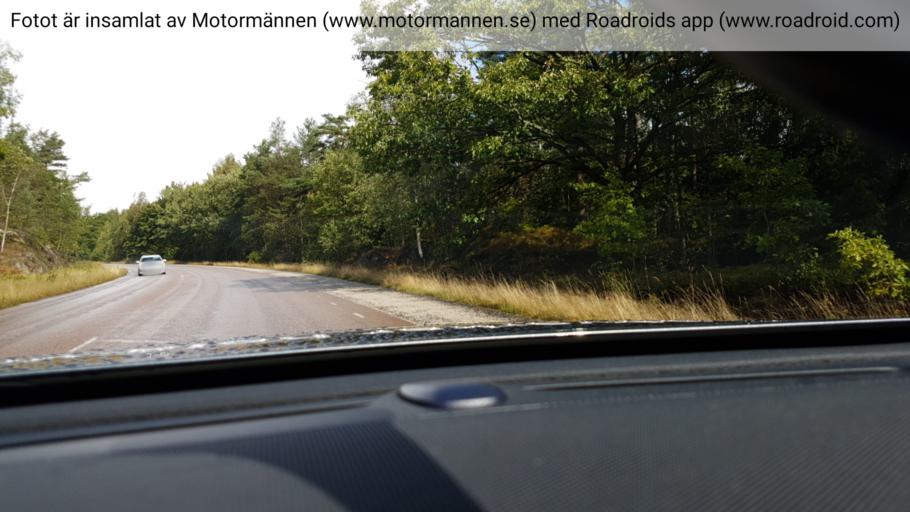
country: SE
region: Vaestra Goetaland
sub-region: Vanersborgs Kommun
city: Vanersborg
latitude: 58.3871
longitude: 12.3051
